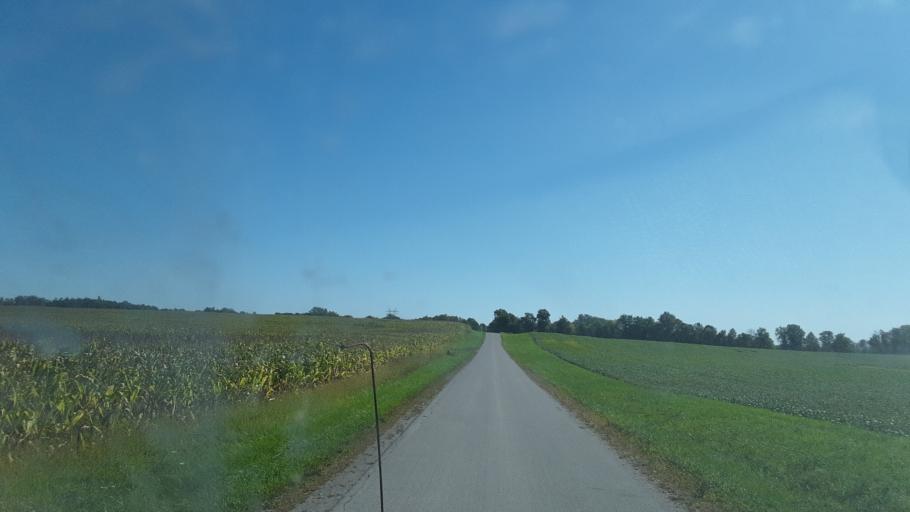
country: US
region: Ohio
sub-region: Wyandot County
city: Upper Sandusky
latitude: 40.9350
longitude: -83.2050
